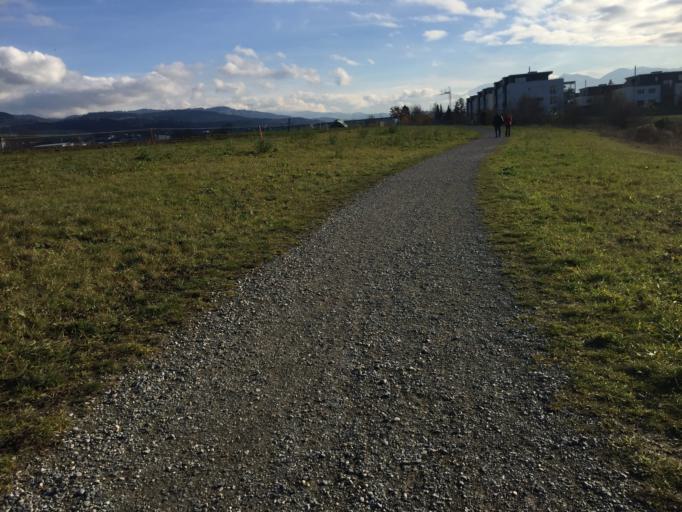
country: CH
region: Bern
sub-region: Bern-Mittelland District
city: Munsingen
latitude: 46.8787
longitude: 7.5487
